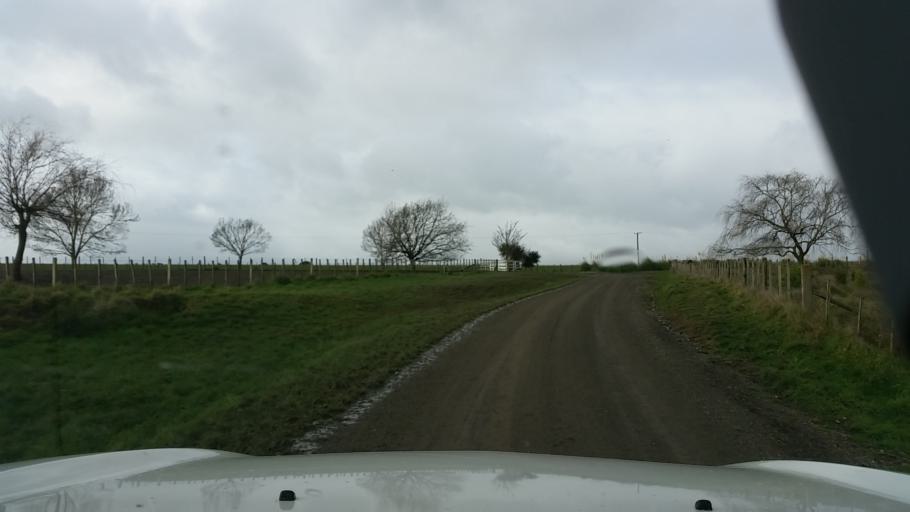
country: NZ
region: Wellington
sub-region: Masterton District
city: Masterton
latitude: -41.1069
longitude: 175.5412
